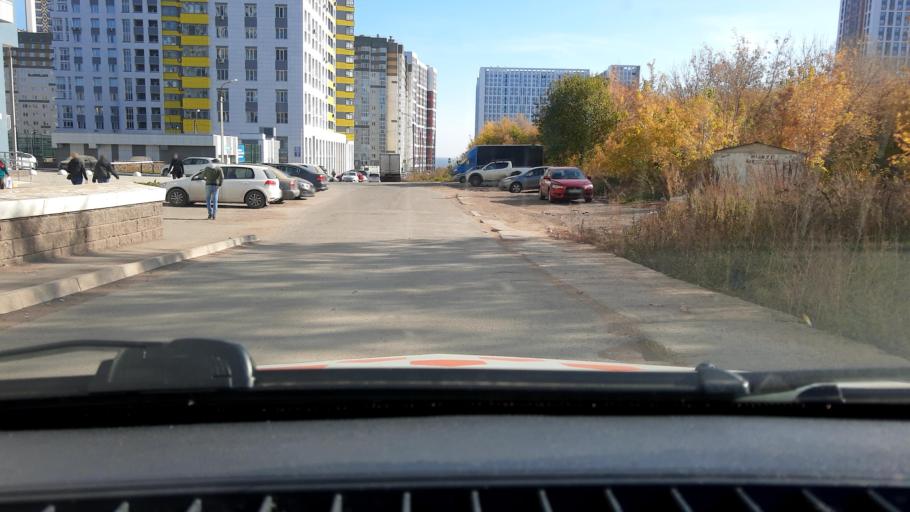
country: RU
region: Bashkortostan
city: Ufa
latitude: 54.7639
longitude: 56.0287
